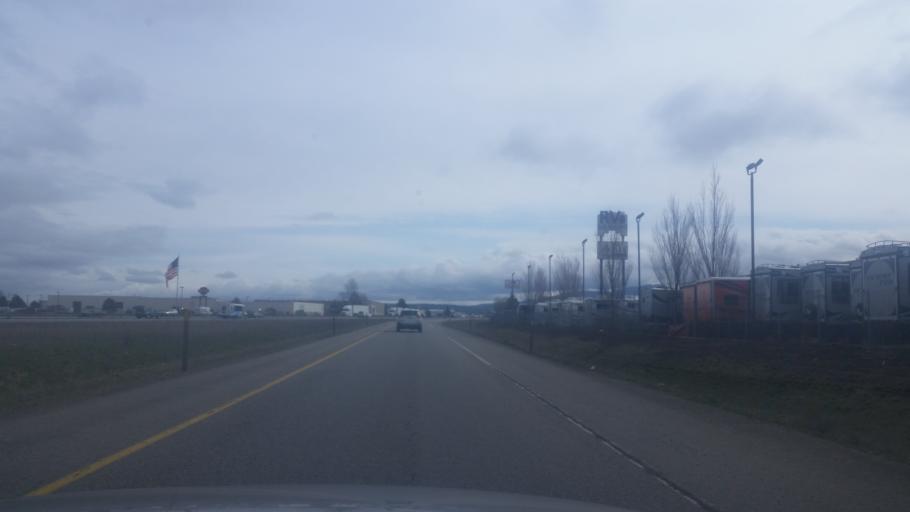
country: US
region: Washington
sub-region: Spokane County
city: Liberty Lake
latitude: 47.6649
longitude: -117.1523
